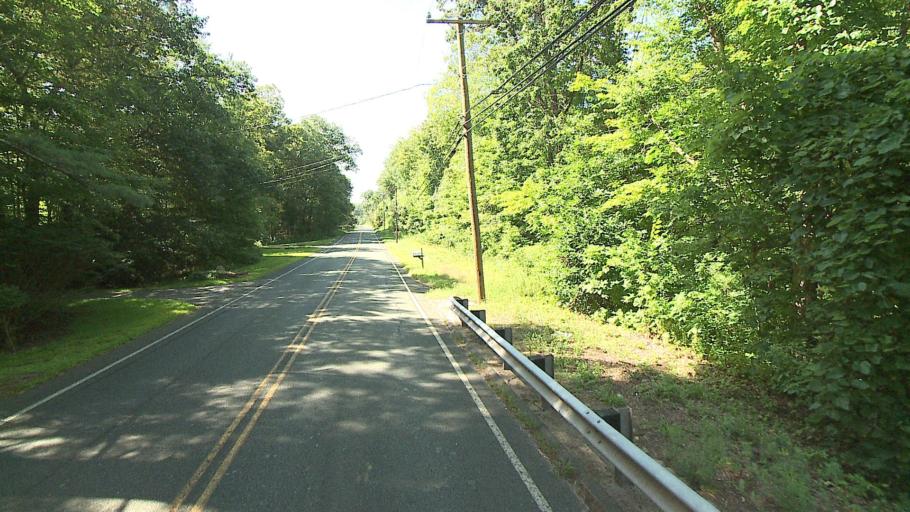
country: US
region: Connecticut
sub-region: Hartford County
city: West Simsbury
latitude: 41.8773
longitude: -72.8634
